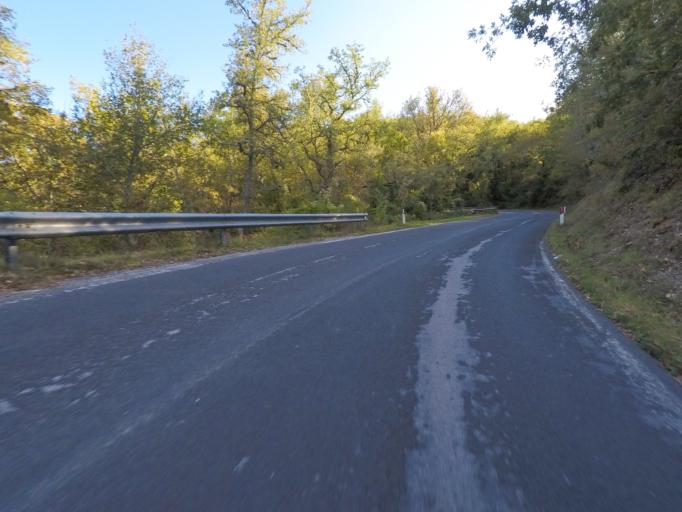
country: IT
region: Tuscany
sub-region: Provincia di Siena
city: Radda in Chianti
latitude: 43.4649
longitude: 11.3819
